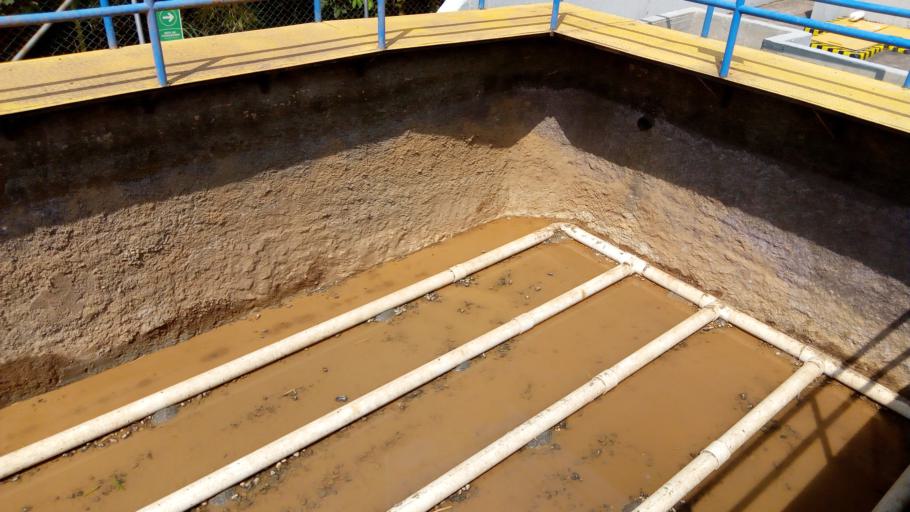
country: CO
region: Valle del Cauca
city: Cali
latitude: 3.4698
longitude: -76.5515
